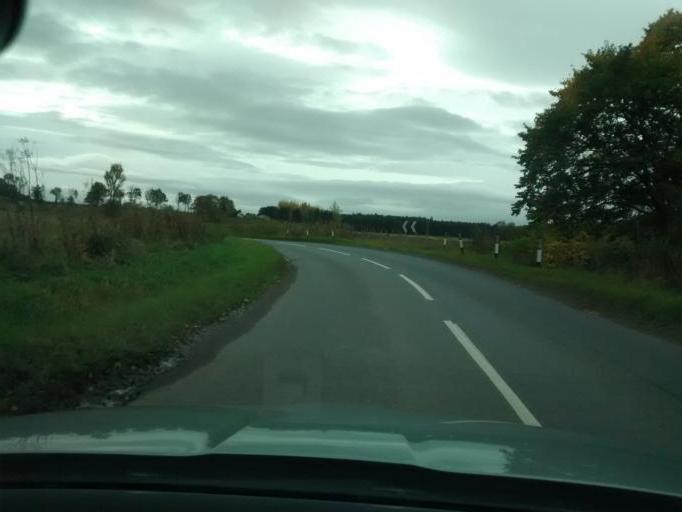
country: GB
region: Scotland
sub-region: Perth and Kinross
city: Stanley
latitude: 56.4991
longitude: -3.4338
